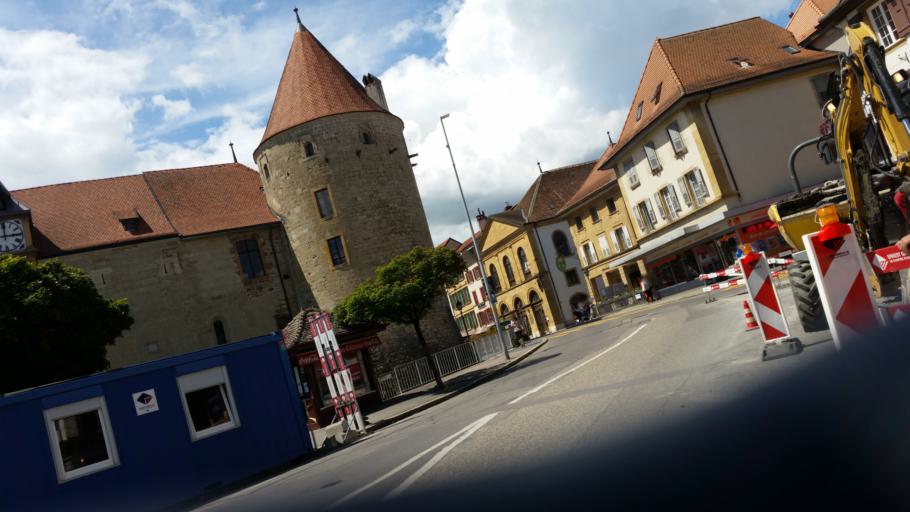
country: CH
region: Vaud
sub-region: Jura-Nord vaudois District
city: Yverdon-les-Bains
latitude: 46.7781
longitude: 6.6423
